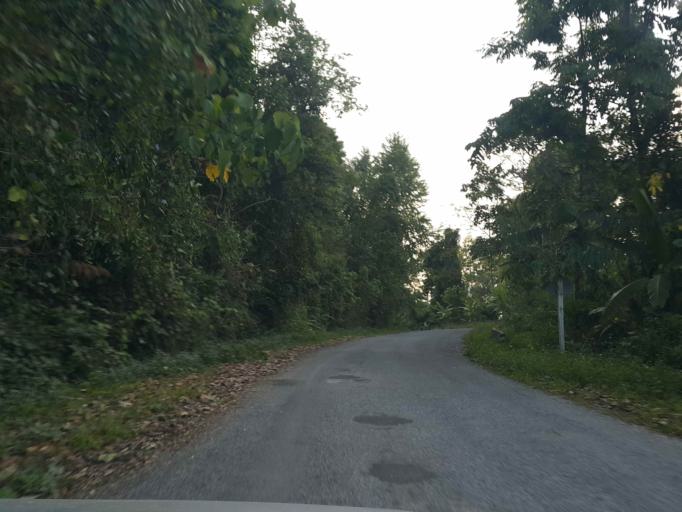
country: TH
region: Chiang Mai
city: Mae On
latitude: 18.9973
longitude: 99.3358
